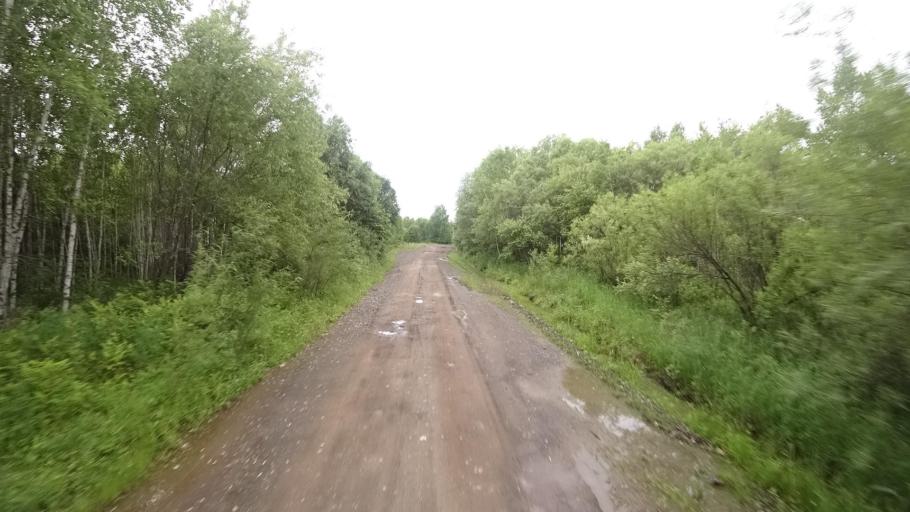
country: RU
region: Khabarovsk Krai
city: Amursk
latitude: 49.9132
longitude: 136.1587
